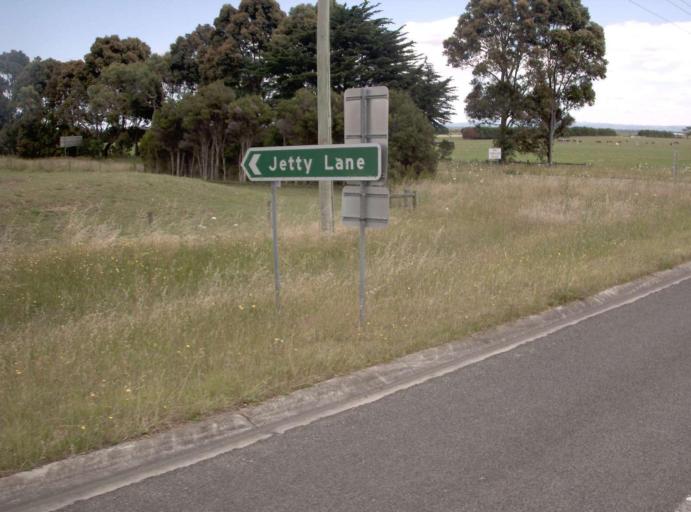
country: AU
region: Victoria
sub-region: Cardinia
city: Koo-Wee-Rup
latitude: -38.3098
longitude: 145.5412
